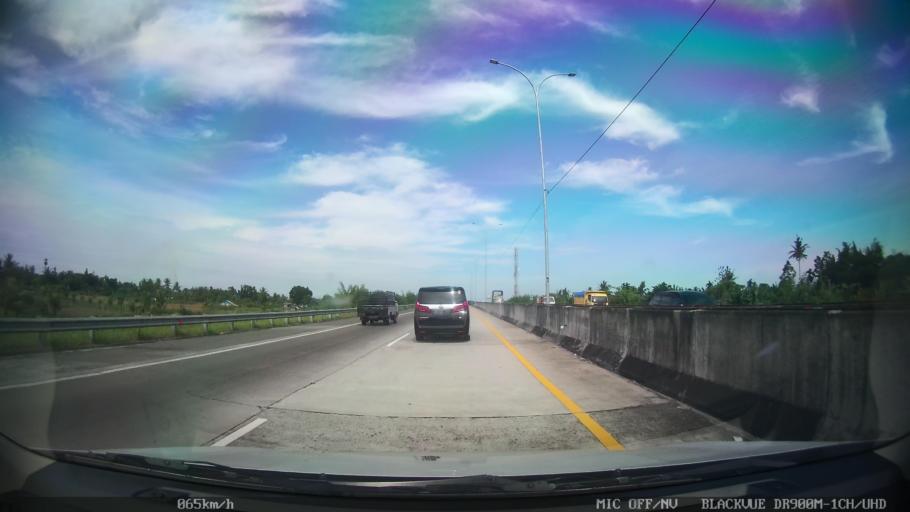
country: ID
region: North Sumatra
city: Binjai
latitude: 3.6454
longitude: 98.5546
